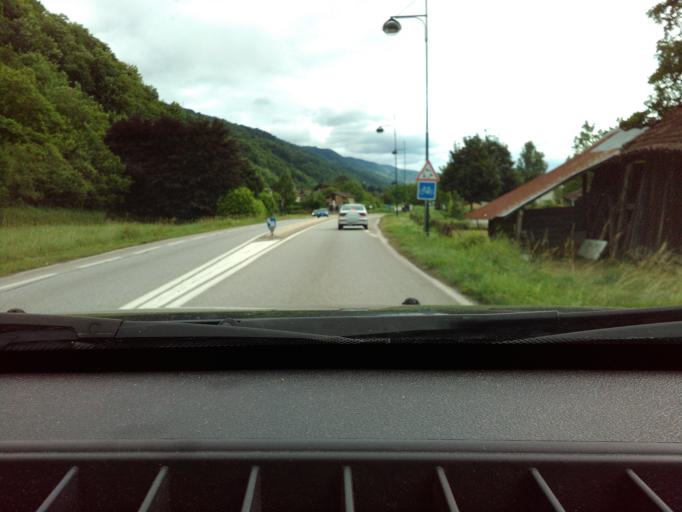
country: FR
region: Rhone-Alpes
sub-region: Departement de l'Isere
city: Tencin
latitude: 45.3159
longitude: 5.9645
